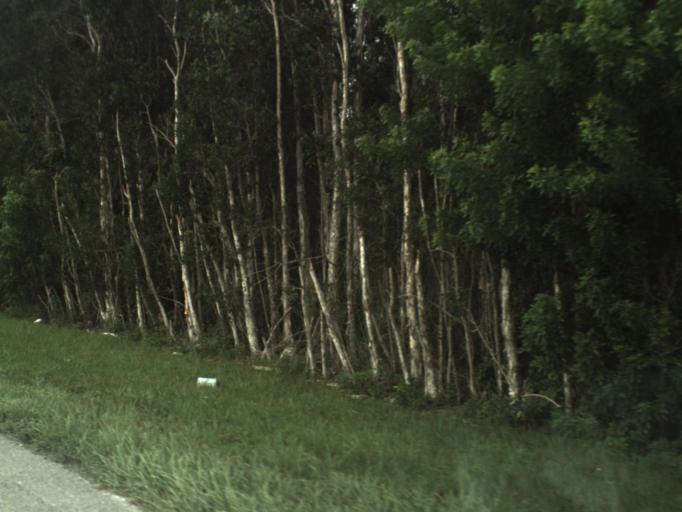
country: US
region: Florida
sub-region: Miami-Dade County
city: Kendall West
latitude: 25.7489
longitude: -80.4810
